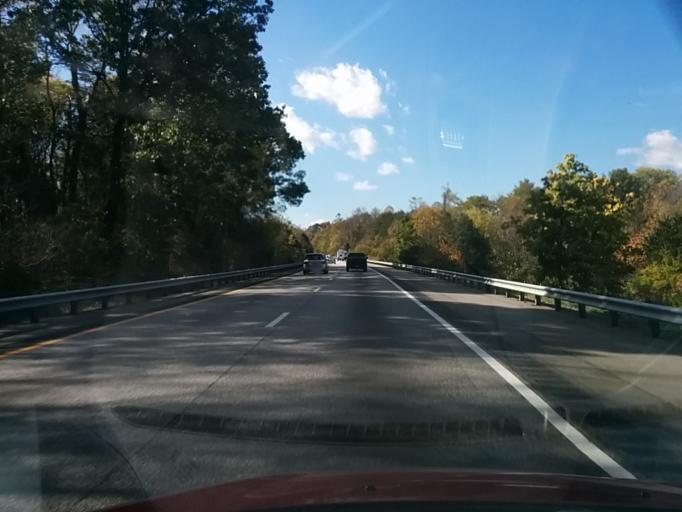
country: US
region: Virginia
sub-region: Botetourt County
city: Fincastle
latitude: 37.4468
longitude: -79.8598
